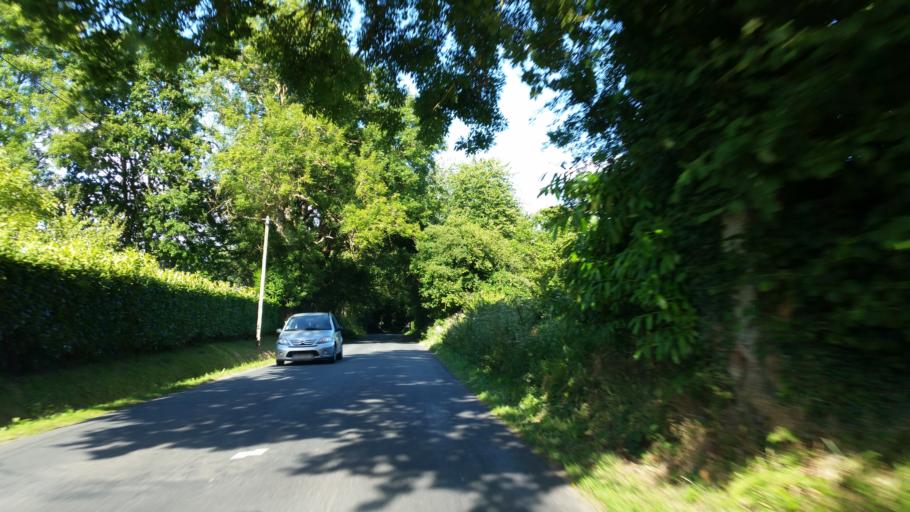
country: FR
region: Lower Normandy
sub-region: Departement du Calvados
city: Saint-Gatien-des-Bois
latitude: 49.3630
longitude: 0.1943
